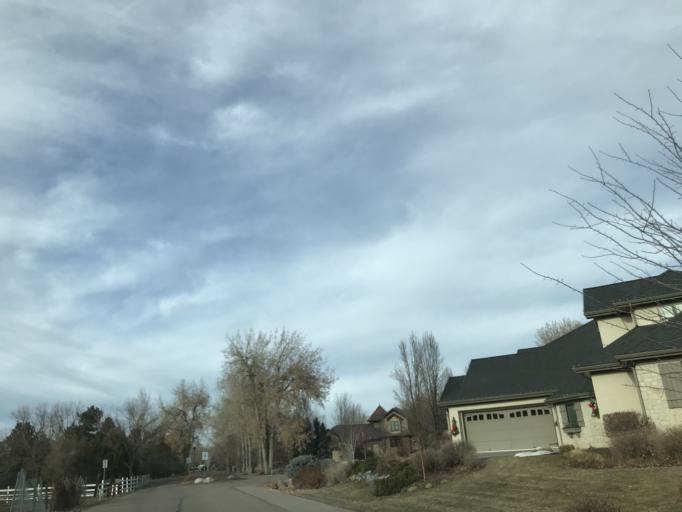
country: US
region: Colorado
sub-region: Arapahoe County
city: Columbine Valley
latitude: 39.6075
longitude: -105.0284
